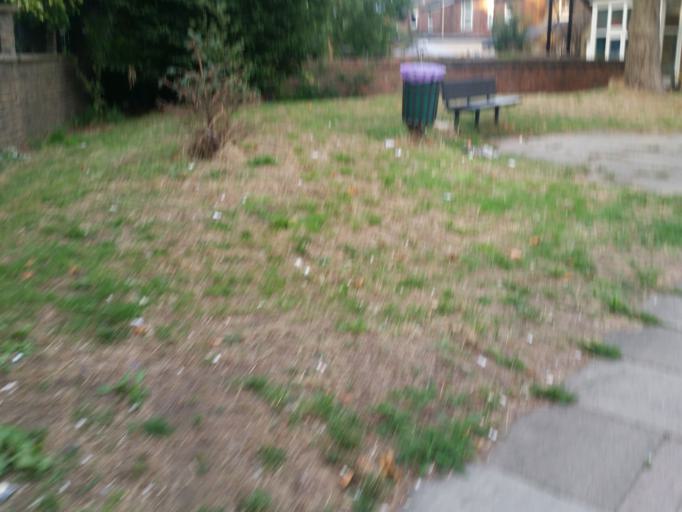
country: GB
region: England
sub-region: Greater London
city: Wood Green
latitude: 51.5893
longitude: -0.1105
